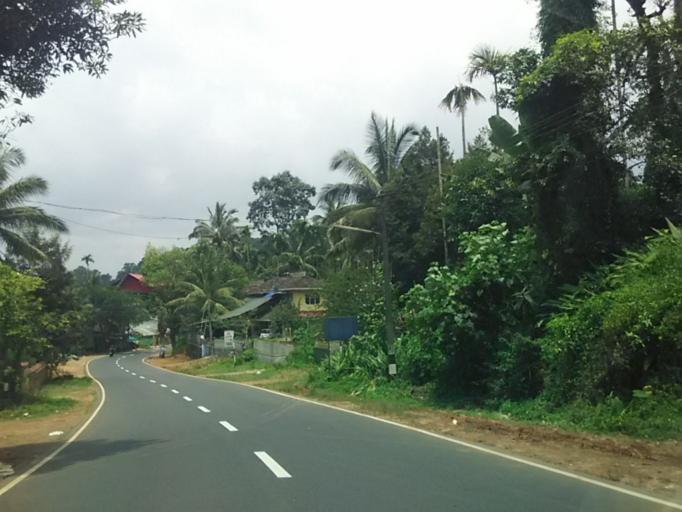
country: IN
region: Kerala
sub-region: Wayanad
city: Kalpetta
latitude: 11.5390
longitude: 76.0360
